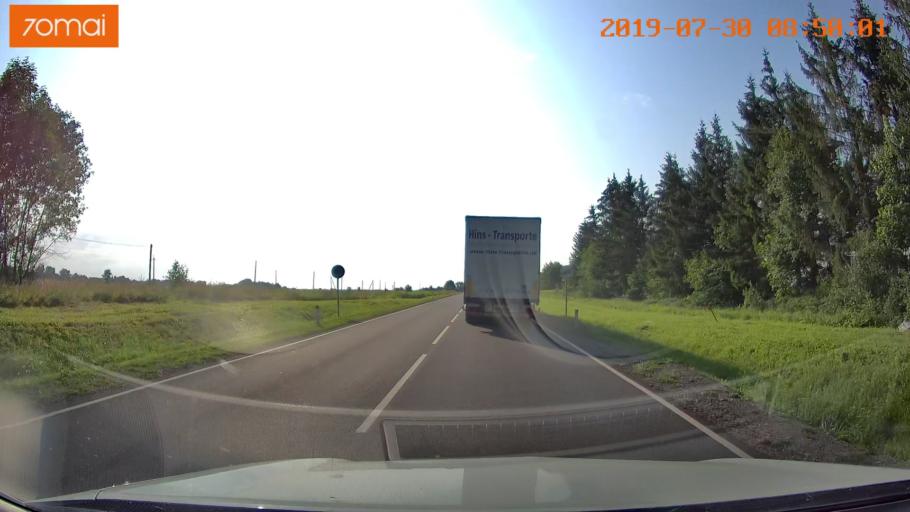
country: RU
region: Kaliningrad
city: Chernyakhovsk
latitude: 54.6098
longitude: 21.9321
